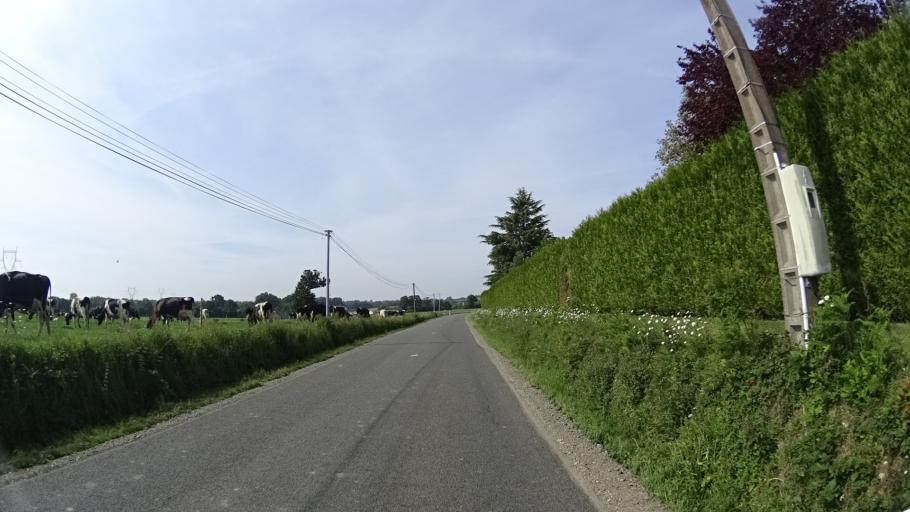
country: FR
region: Brittany
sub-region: Departement d'Ille-et-Vilaine
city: Nouvoitou
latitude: 48.0274
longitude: -1.5346
